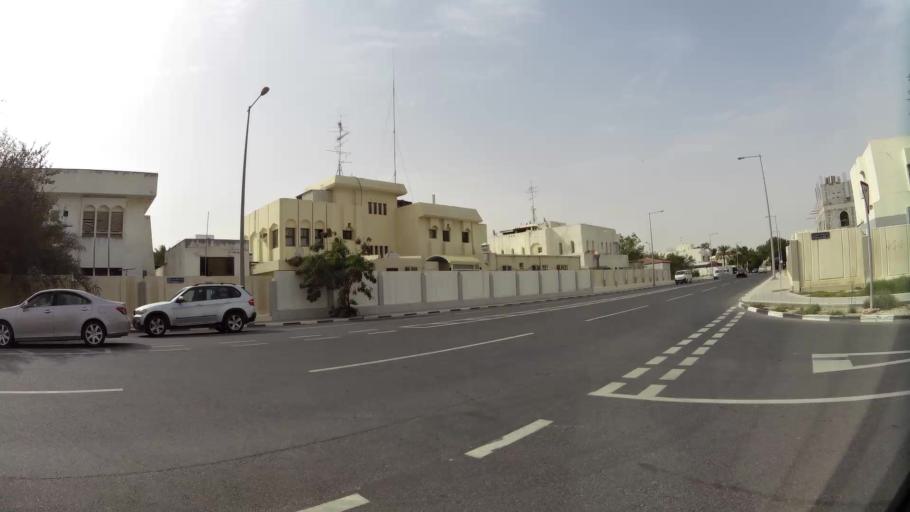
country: QA
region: Baladiyat ad Dawhah
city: Doha
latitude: 25.3239
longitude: 51.5067
